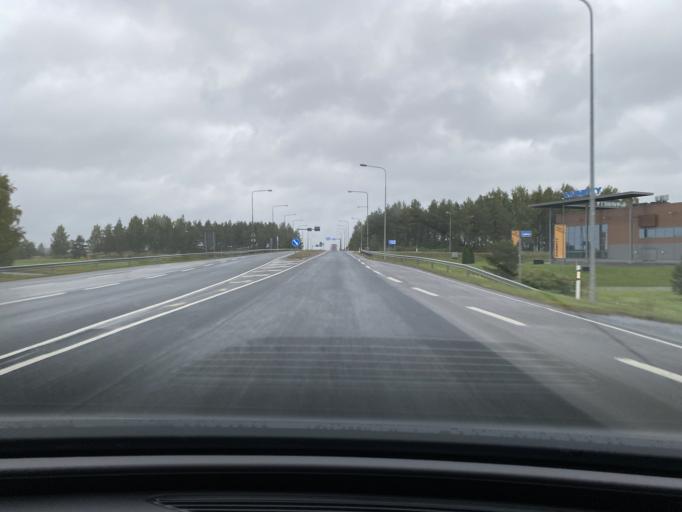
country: FI
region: Satakunta
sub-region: Pori
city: Huittinen
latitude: 61.1672
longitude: 22.6743
